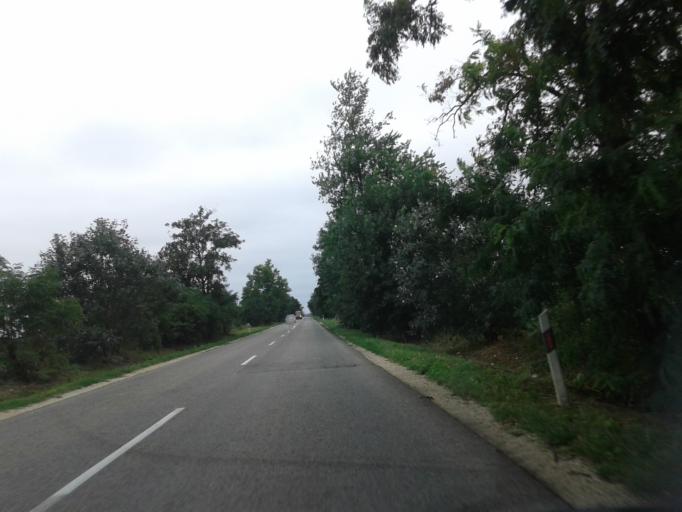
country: HU
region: Pest
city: Domsod
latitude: 47.0646
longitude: 19.0142
